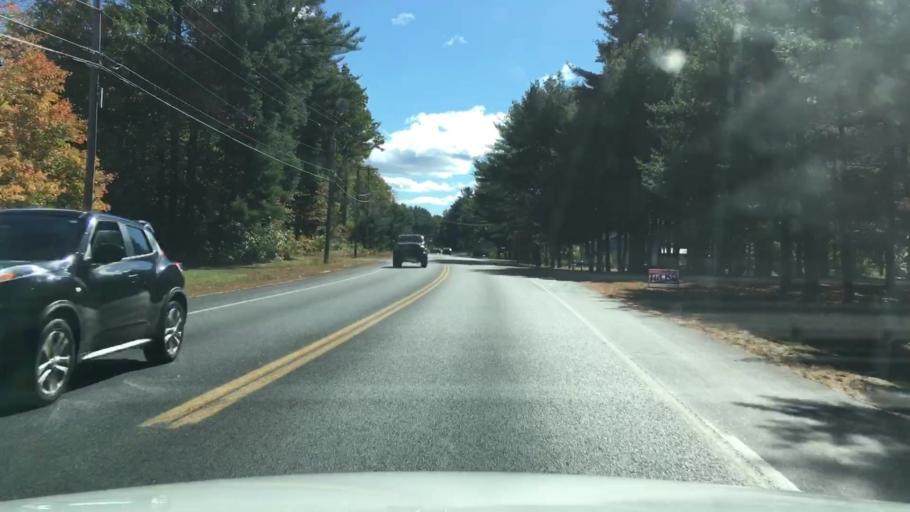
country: US
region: Maine
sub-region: York County
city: South Sanford
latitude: 43.4328
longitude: -70.7337
